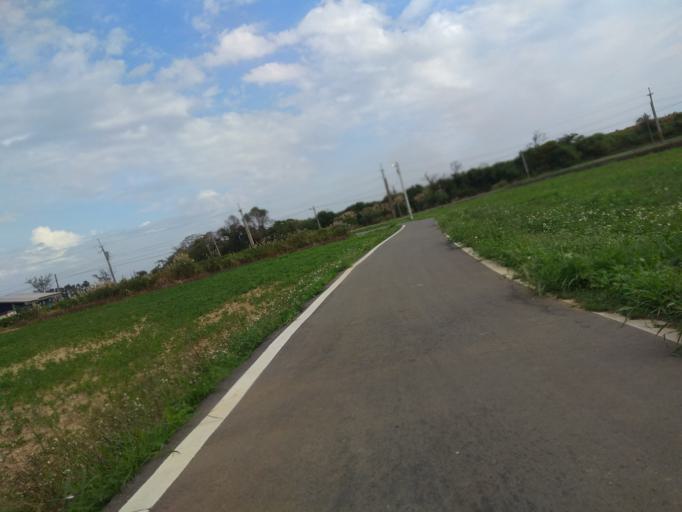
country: TW
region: Taiwan
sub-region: Hsinchu
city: Zhubei
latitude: 24.9493
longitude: 121.0047
